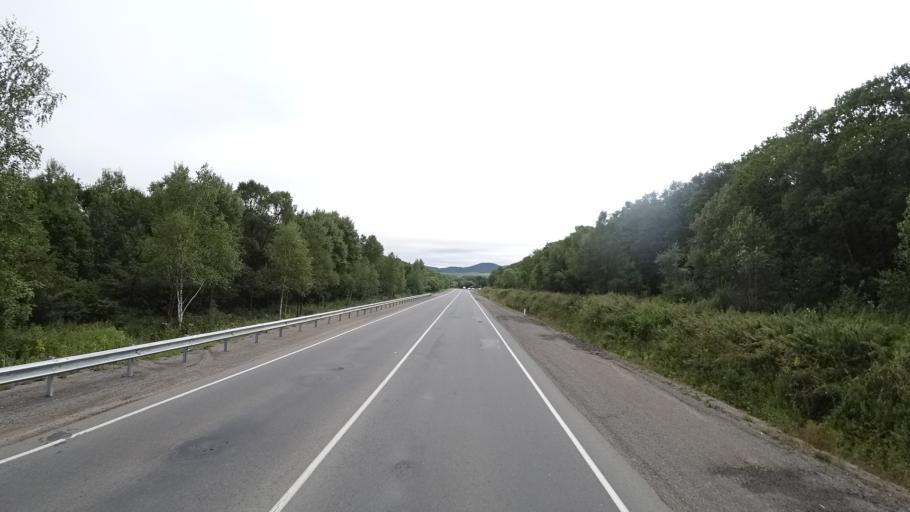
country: RU
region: Primorskiy
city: Lyalichi
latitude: 44.1030
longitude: 132.4237
